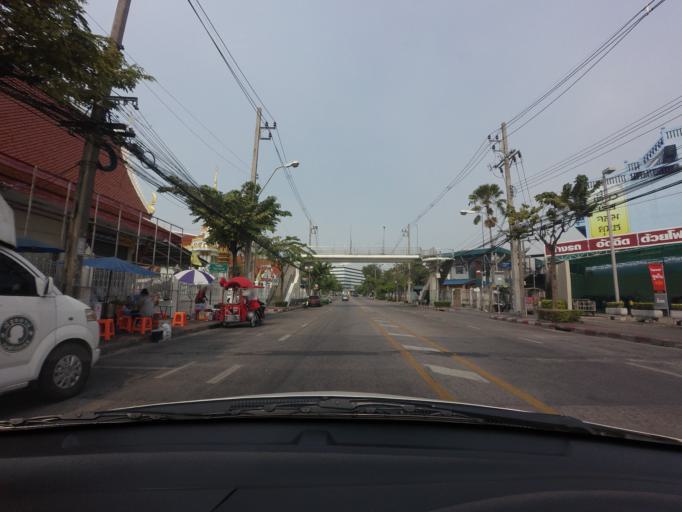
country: TH
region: Bangkok
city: Taling Chan
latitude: 13.7753
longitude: 100.4660
